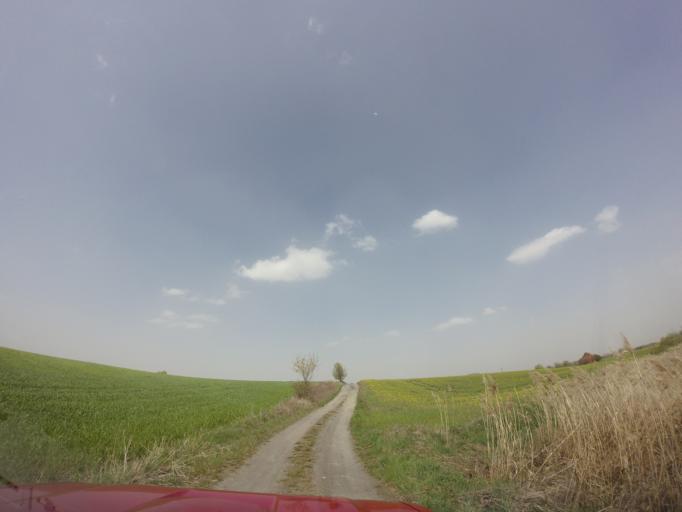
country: PL
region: West Pomeranian Voivodeship
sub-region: Powiat choszczenski
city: Drawno
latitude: 53.2183
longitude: 15.7463
